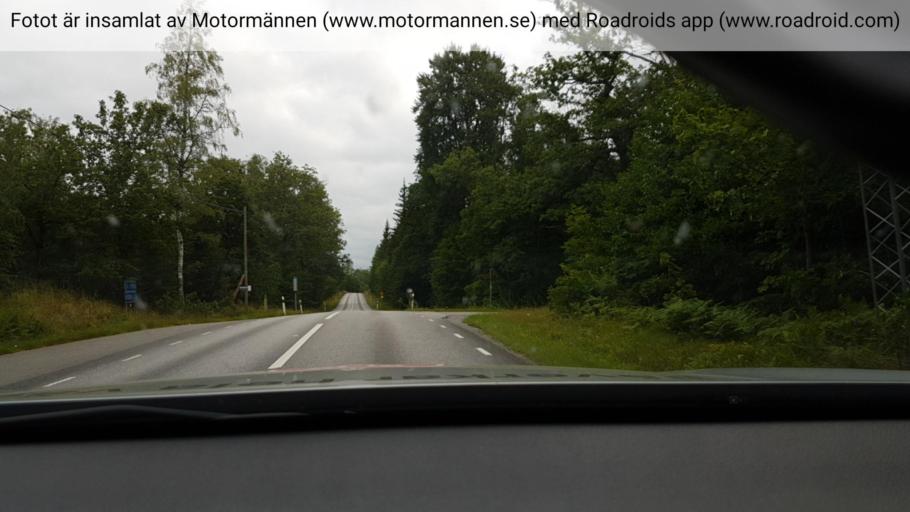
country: SE
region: Stockholm
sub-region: Norrtalje Kommun
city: Skanninge
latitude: 59.8584
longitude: 18.4492
